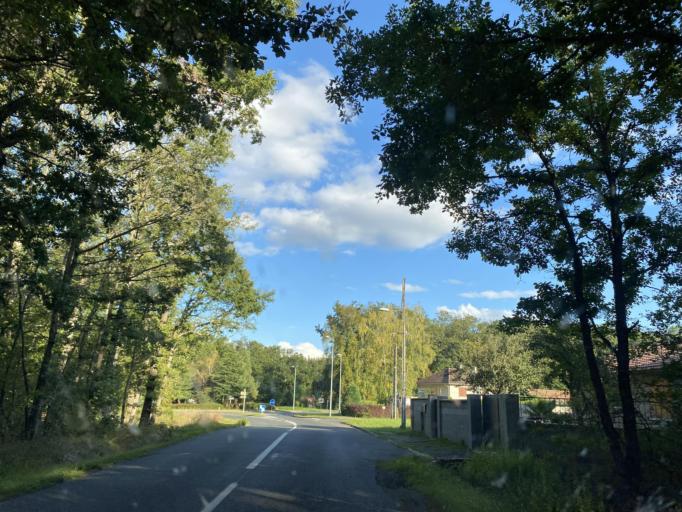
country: FR
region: Auvergne
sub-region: Departement du Puy-de-Dome
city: Randan
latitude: 46.0265
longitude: 3.3530
